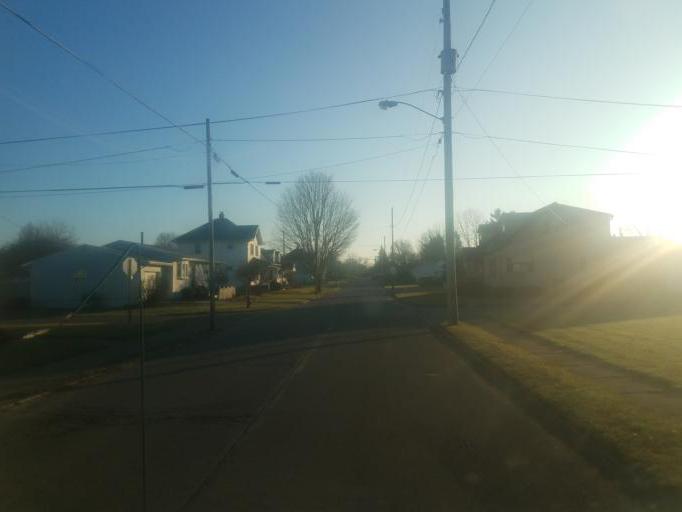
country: US
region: Ohio
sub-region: Crawford County
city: Bucyrus
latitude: 40.8196
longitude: -82.9690
